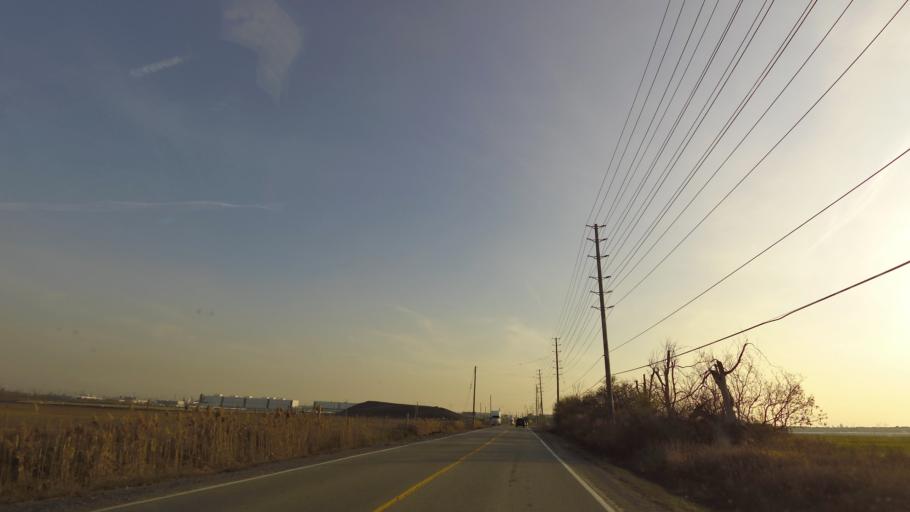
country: CA
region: Ontario
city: Brampton
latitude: 43.7898
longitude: -79.6519
